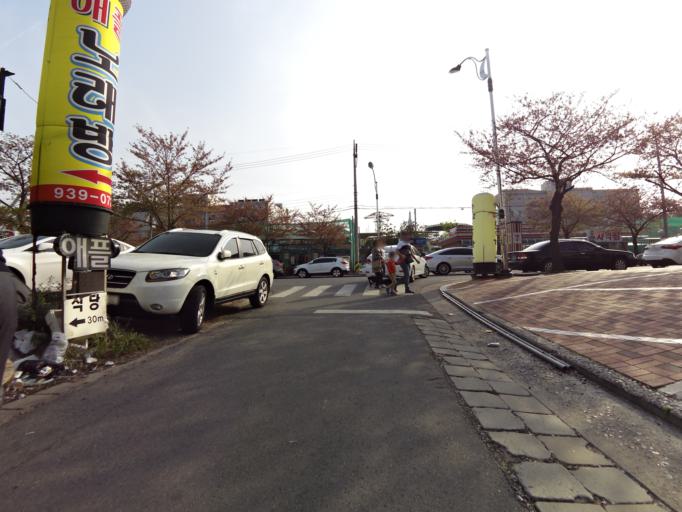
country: KR
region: Daegu
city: Daegu
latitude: 35.8793
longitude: 128.6541
